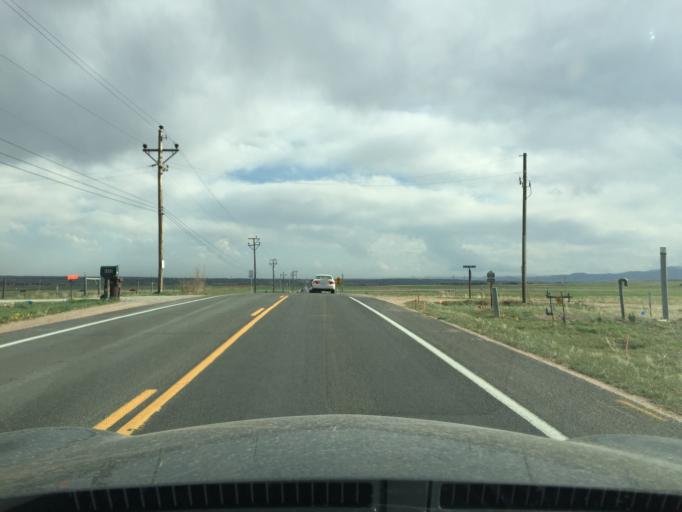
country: US
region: Colorado
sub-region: Boulder County
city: Niwot
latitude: 40.0912
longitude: -105.1316
